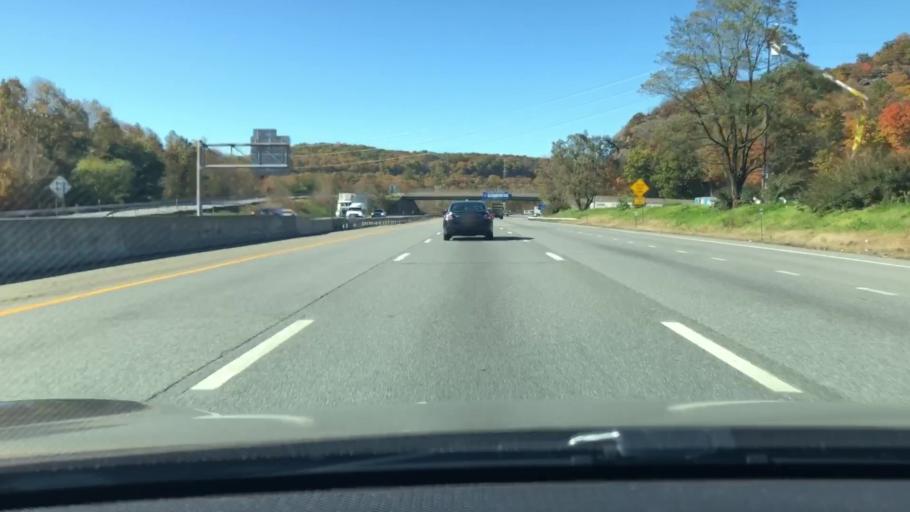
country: US
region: New York
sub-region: Rockland County
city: Sloatsburg
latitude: 41.1429
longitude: -74.1782
